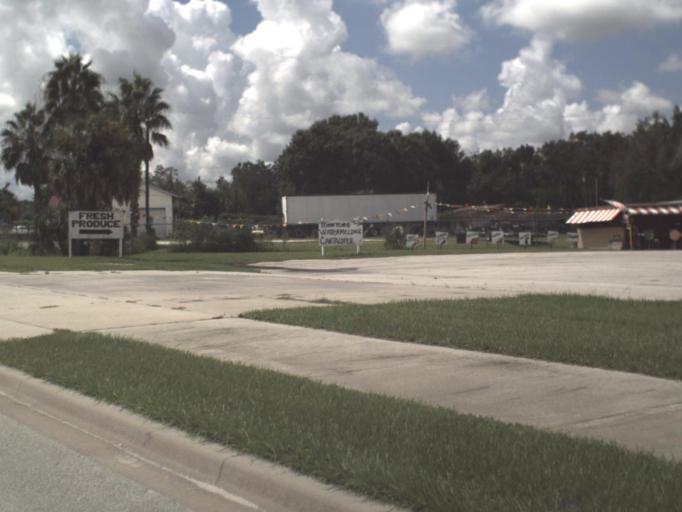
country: US
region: Florida
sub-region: Hardee County
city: Zolfo Springs
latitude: 27.4984
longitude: -81.7969
